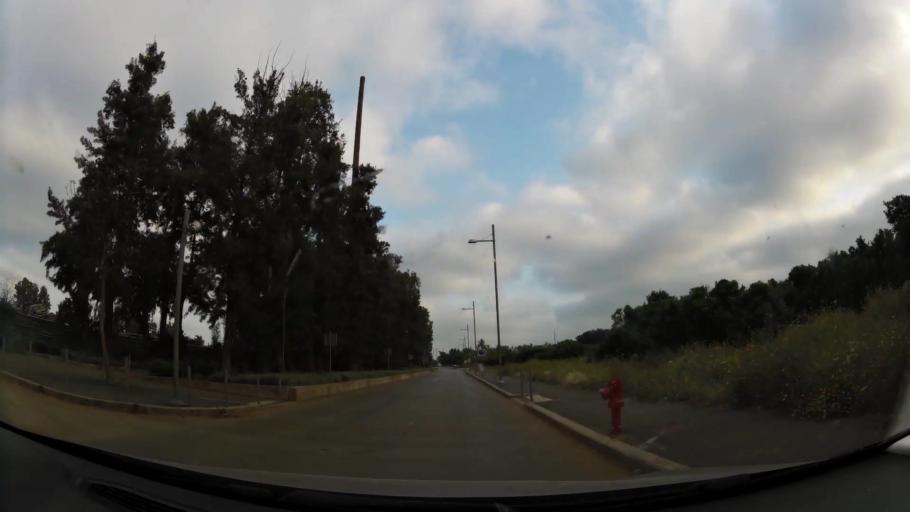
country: MA
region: Rabat-Sale-Zemmour-Zaer
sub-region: Rabat
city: Rabat
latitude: 33.9498
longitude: -6.8329
